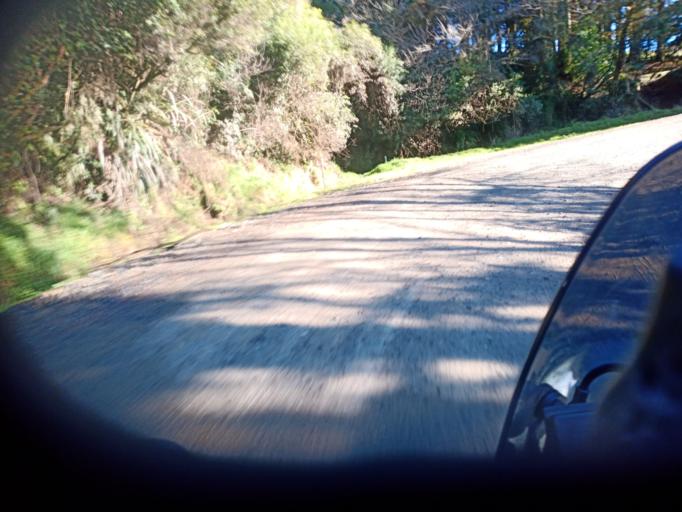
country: NZ
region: Gisborne
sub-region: Gisborne District
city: Gisborne
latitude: -38.2122
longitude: 178.0653
